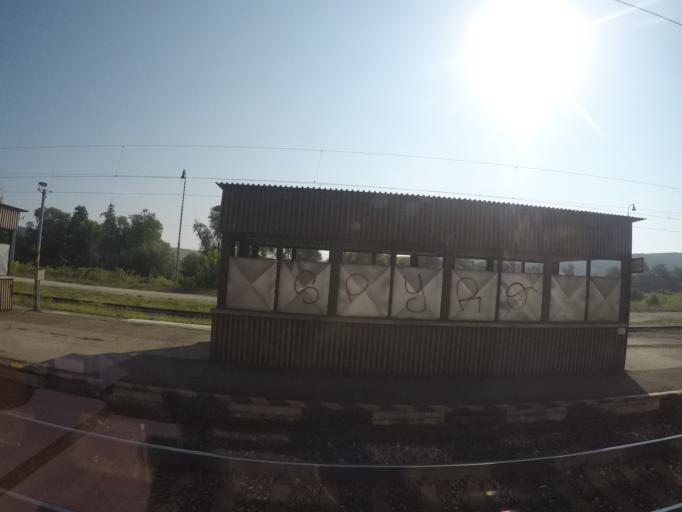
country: SK
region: Kosicky
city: Kosice
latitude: 48.7957
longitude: 21.2460
